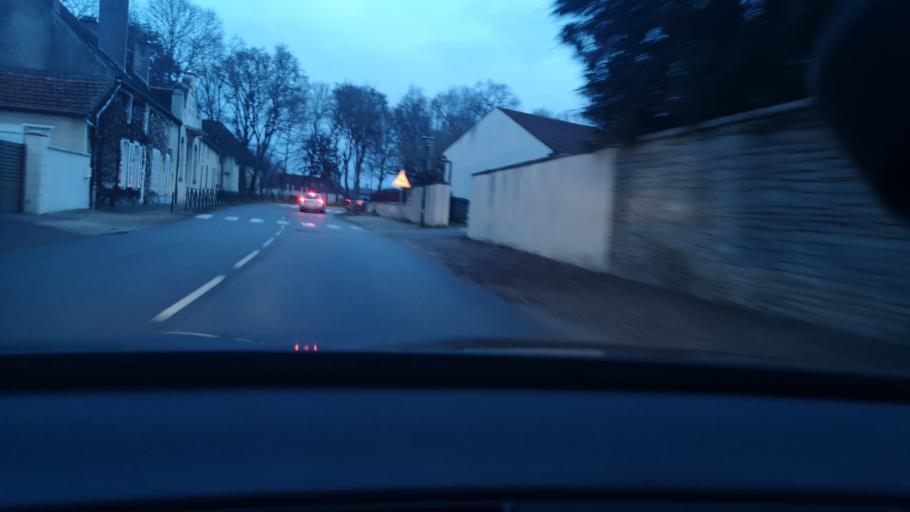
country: FR
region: Bourgogne
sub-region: Departement de Saone-et-Loire
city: Demigny
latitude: 46.9463
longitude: 4.9097
